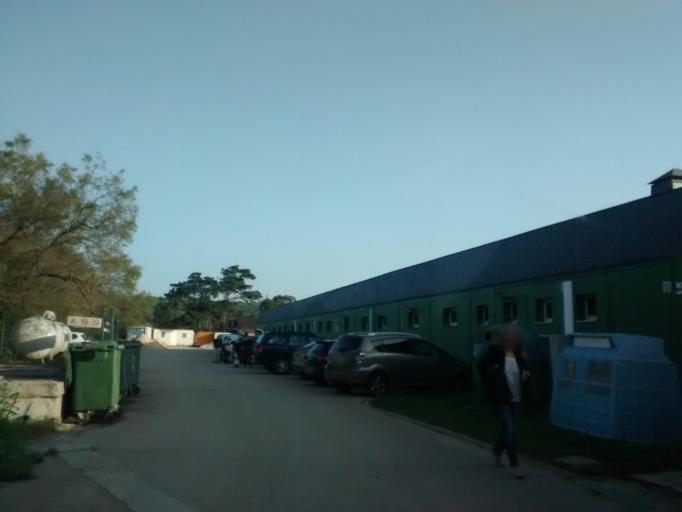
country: ES
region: Cantabria
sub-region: Provincia de Cantabria
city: Miengo
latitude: 43.4418
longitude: -3.9597
